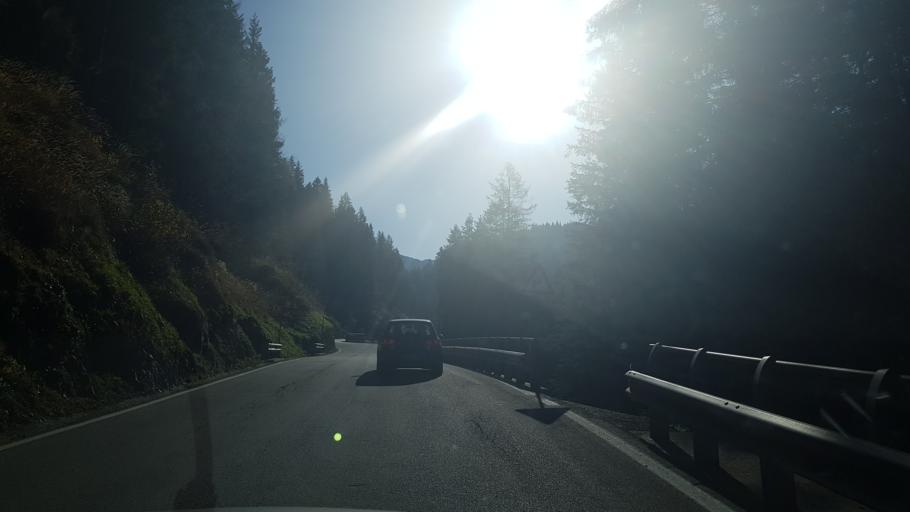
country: IT
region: Veneto
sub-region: Provincia di Belluno
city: Sappada
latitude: 46.5752
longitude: 12.6474
